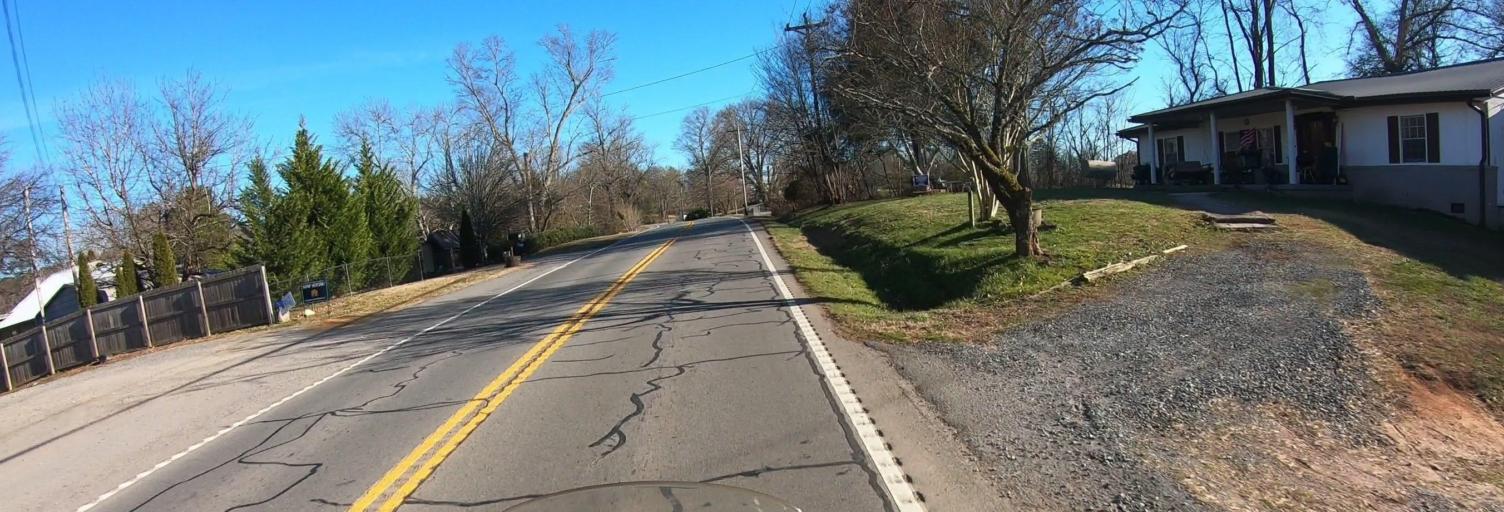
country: US
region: Georgia
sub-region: Fannin County
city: Blue Ridge
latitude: 34.9261
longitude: -84.2875
